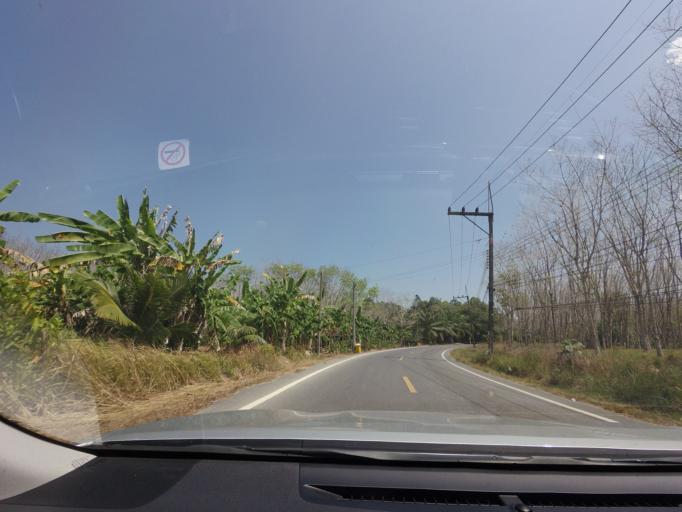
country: TH
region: Phangnga
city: Takua Thung
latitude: 8.2513
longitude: 98.3968
